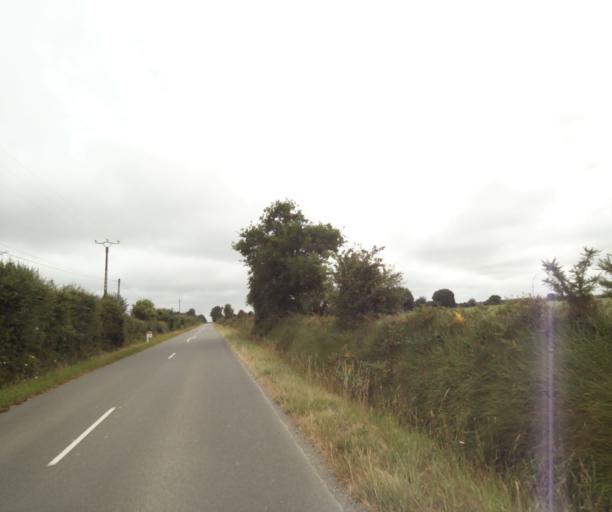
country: FR
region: Pays de la Loire
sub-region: Departement de la Vendee
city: Sainte-Foy
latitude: 46.5026
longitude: -1.6925
